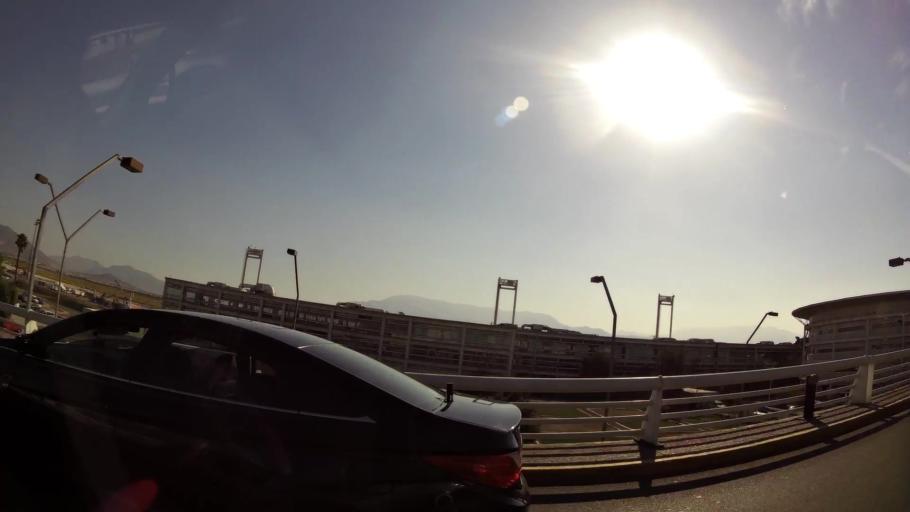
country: CL
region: Santiago Metropolitan
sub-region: Provincia de Santiago
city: Lo Prado
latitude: -33.3979
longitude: -70.7952
